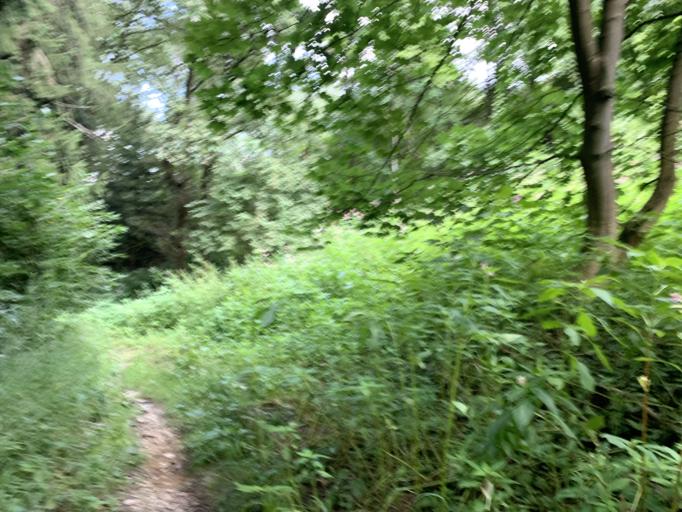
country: DE
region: Bavaria
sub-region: Upper Bavaria
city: Freising
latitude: 48.4174
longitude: 11.7636
